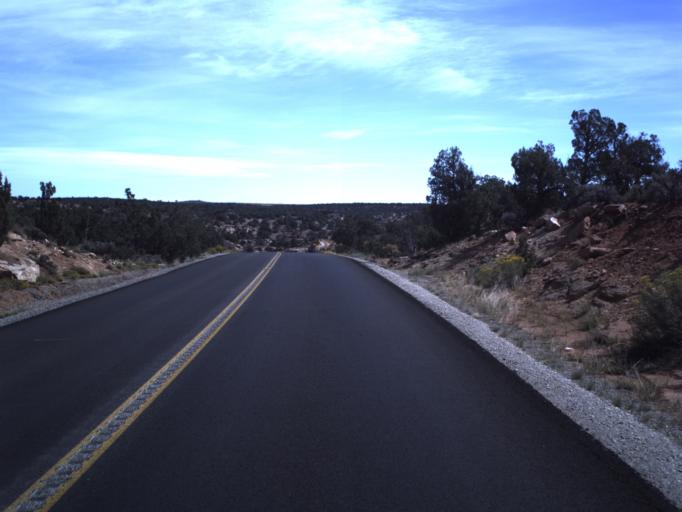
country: US
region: Utah
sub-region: San Juan County
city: Blanding
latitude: 37.5773
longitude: -109.5180
